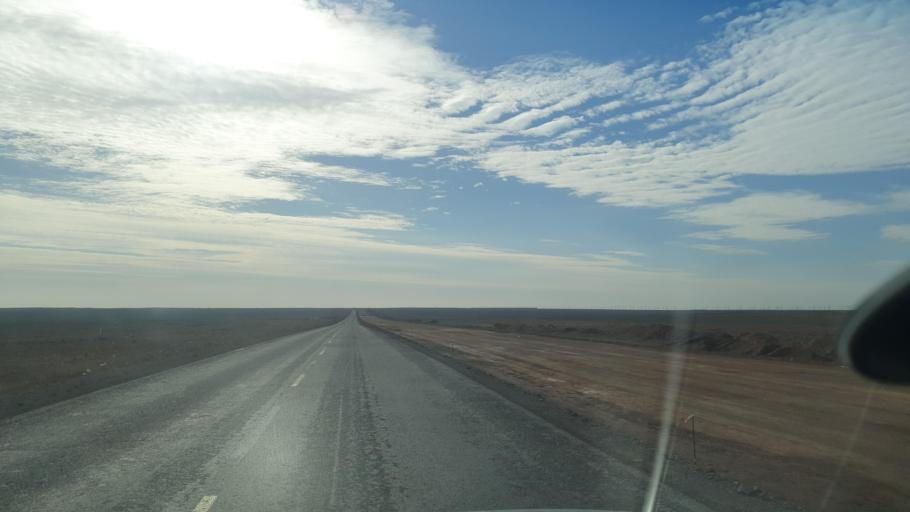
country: KZ
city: Priozersk
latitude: 45.9659
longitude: 73.5459
